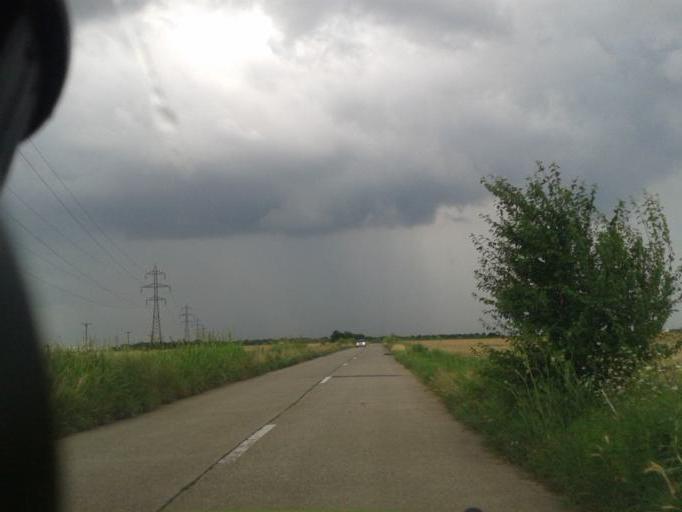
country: RO
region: Calarasi
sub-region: Comuna Belciugatele
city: Belciugatele
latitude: 44.5424
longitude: 26.4540
